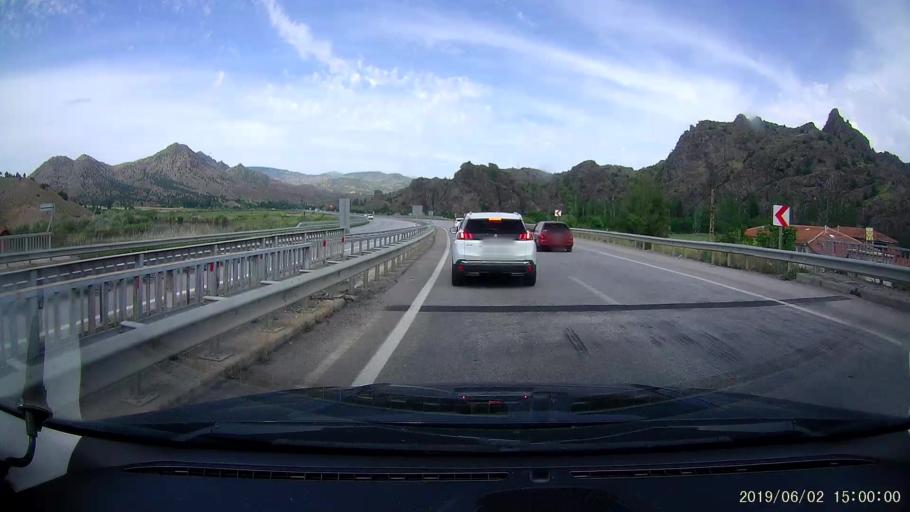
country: TR
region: Corum
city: Osmancik
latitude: 40.9726
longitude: 34.7053
